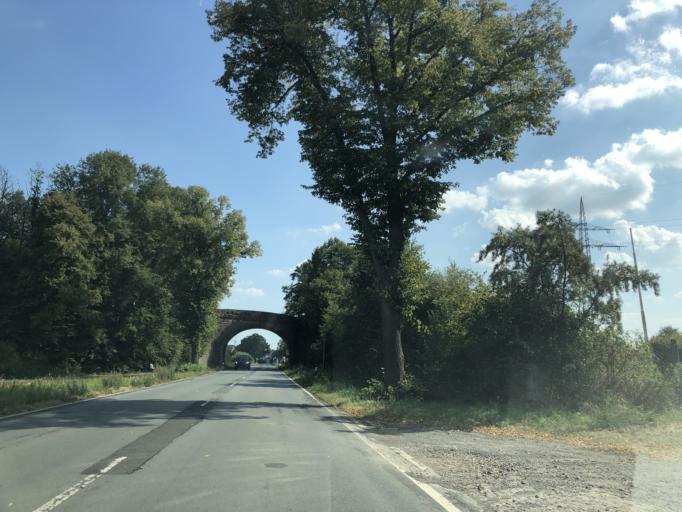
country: DE
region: Hesse
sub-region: Regierungsbezirk Giessen
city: Kirchhain
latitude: 50.8302
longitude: 8.9070
